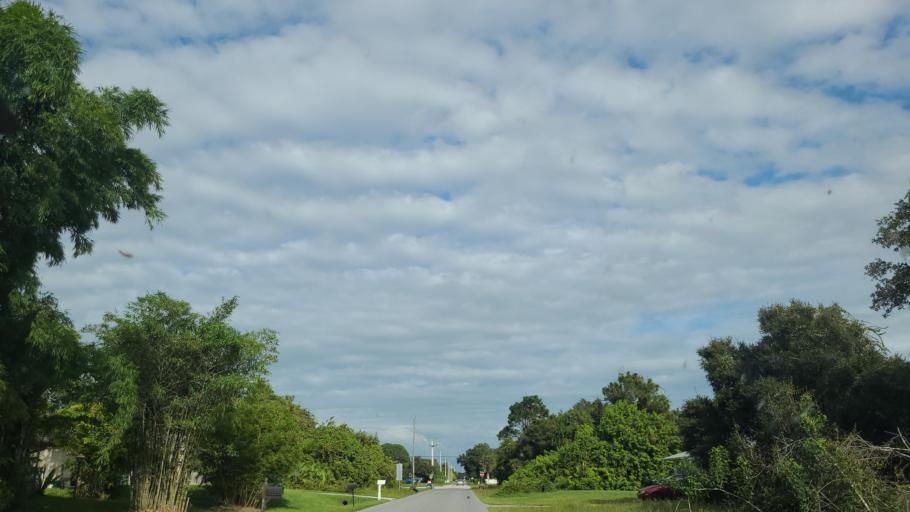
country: US
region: Florida
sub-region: Brevard County
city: Palm Bay
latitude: 27.9836
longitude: -80.6501
